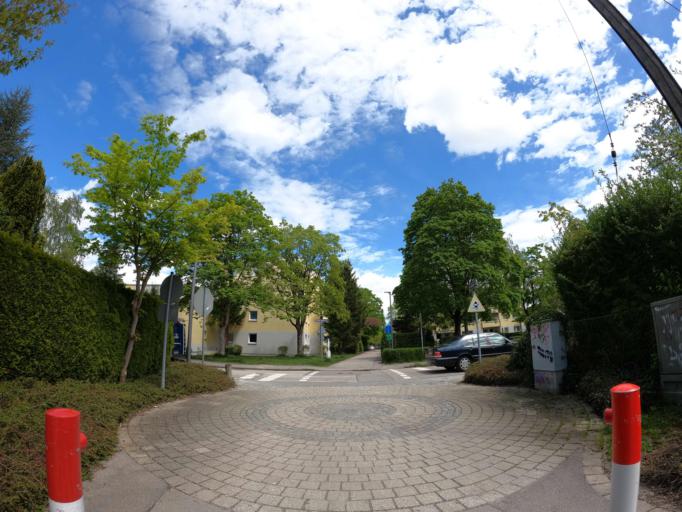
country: DE
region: Bavaria
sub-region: Upper Bavaria
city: Ottobrunn
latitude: 48.0672
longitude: 11.6850
